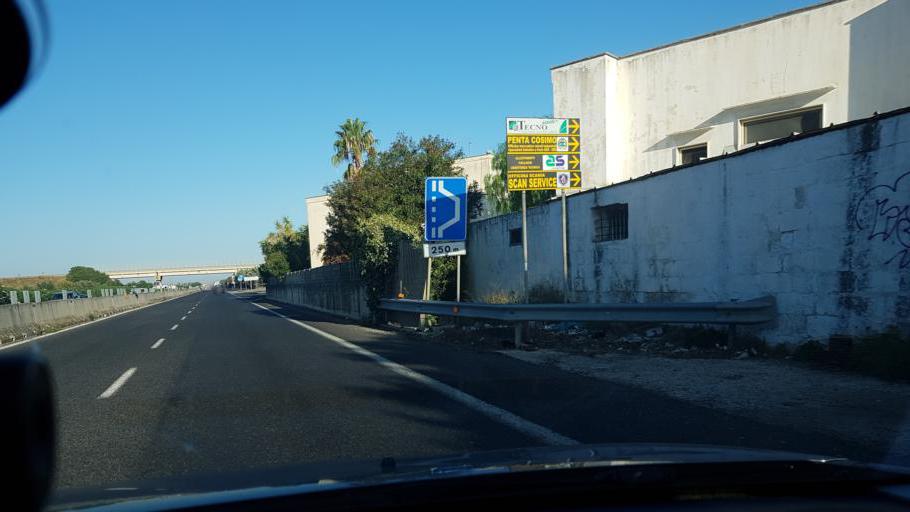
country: IT
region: Apulia
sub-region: Provincia di Bari
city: Monopoli
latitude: 40.9296
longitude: 17.3039
